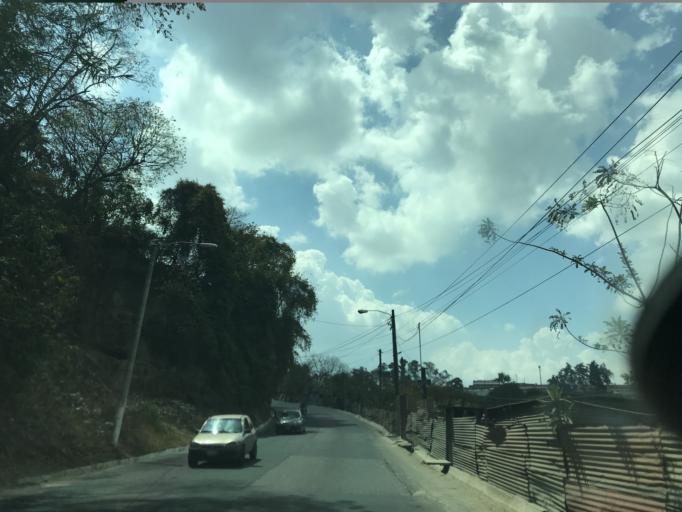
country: GT
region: Guatemala
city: Mixco
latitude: 14.6746
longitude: -90.5731
